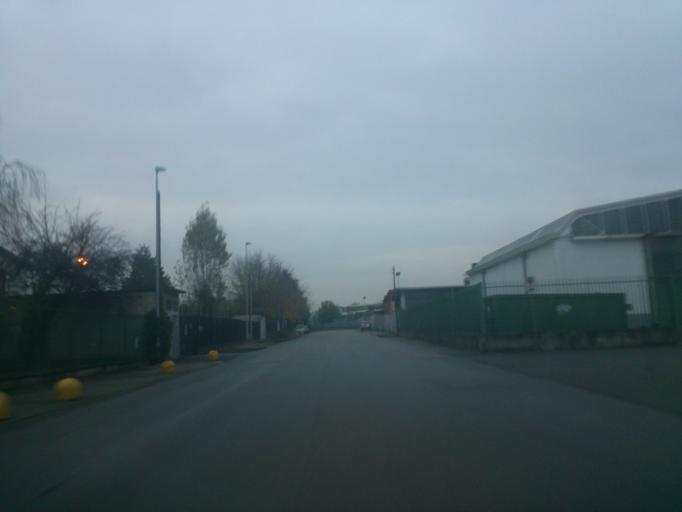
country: IT
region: Lombardy
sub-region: Citta metropolitana di Milano
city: Civesio
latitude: 45.4070
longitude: 9.2595
